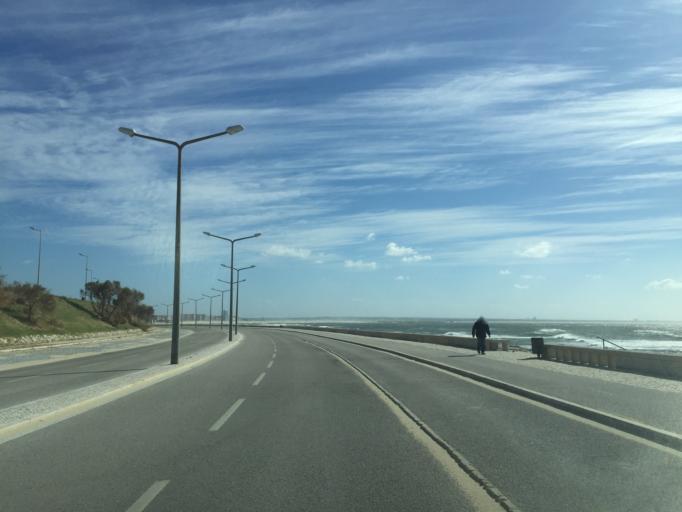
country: PT
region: Coimbra
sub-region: Figueira da Foz
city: Buarcos
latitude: 40.1731
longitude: -8.8941
